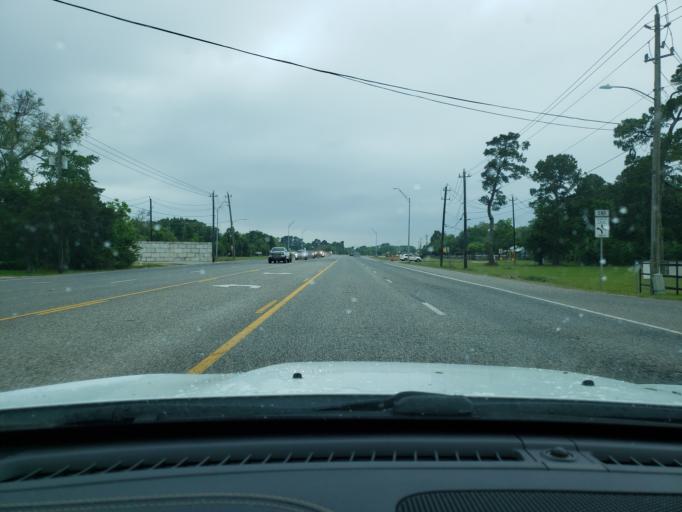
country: US
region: Texas
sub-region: Harris County
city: Baytown
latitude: 29.7642
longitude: -94.9225
